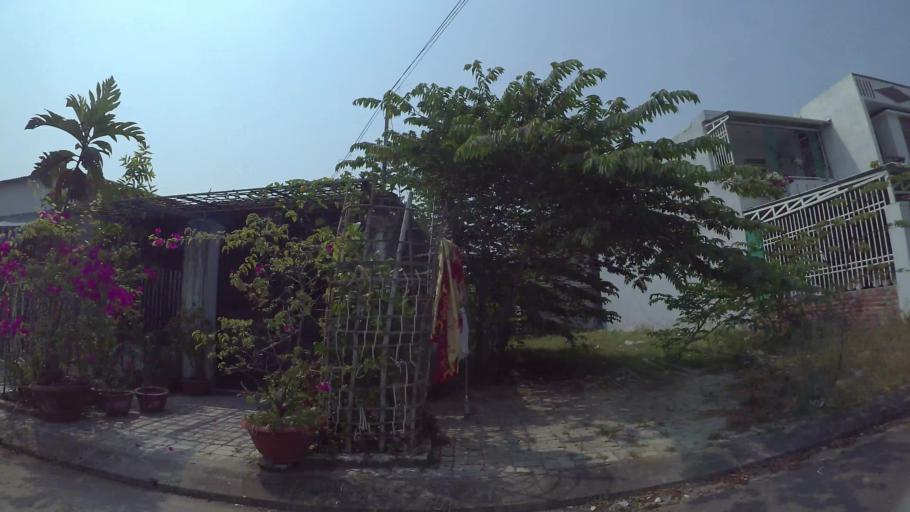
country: VN
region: Da Nang
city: Cam Le
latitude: 15.9703
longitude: 108.2120
